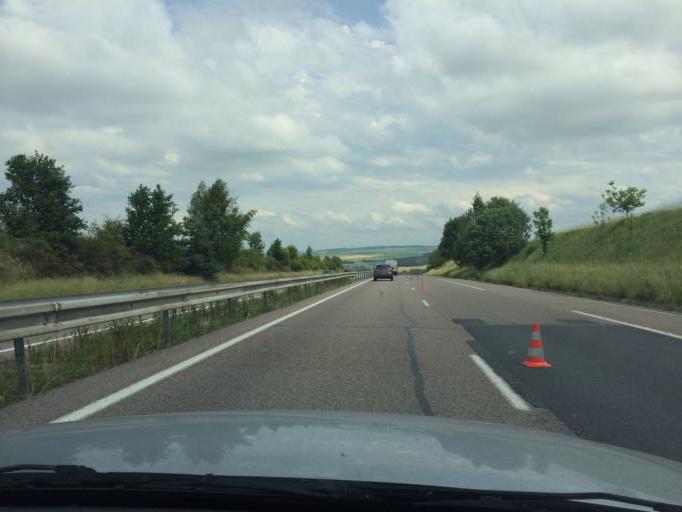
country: FR
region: Champagne-Ardenne
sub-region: Departement de la Marne
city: Dormans
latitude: 49.1491
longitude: 3.6638
